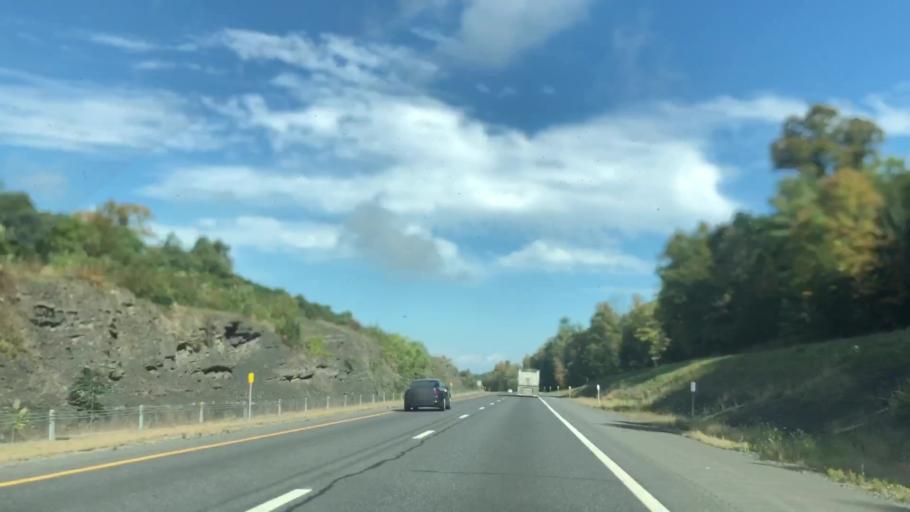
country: US
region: New York
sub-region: Ulster County
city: Tillson
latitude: 41.8001
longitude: -74.0515
